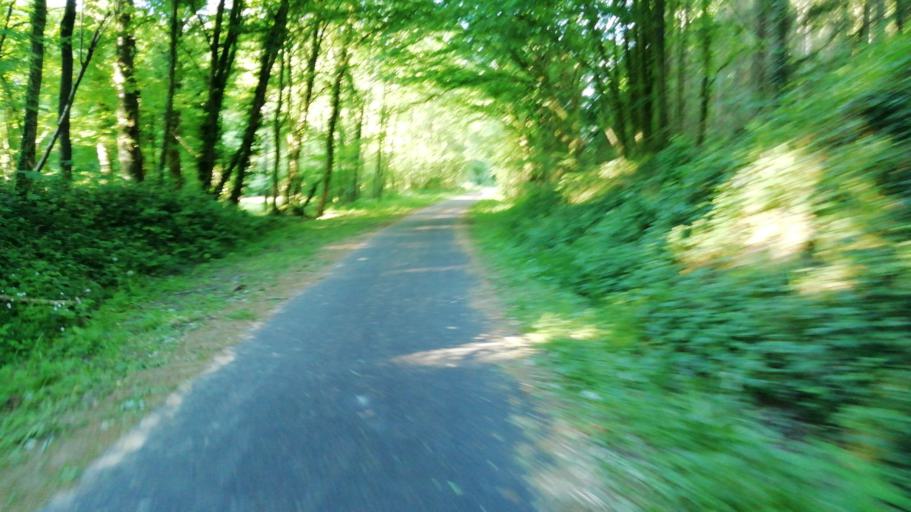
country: FR
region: Nord-Pas-de-Calais
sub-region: Departement du Nord
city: Ferriere-la-Grande
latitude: 50.2022
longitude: 4.0279
